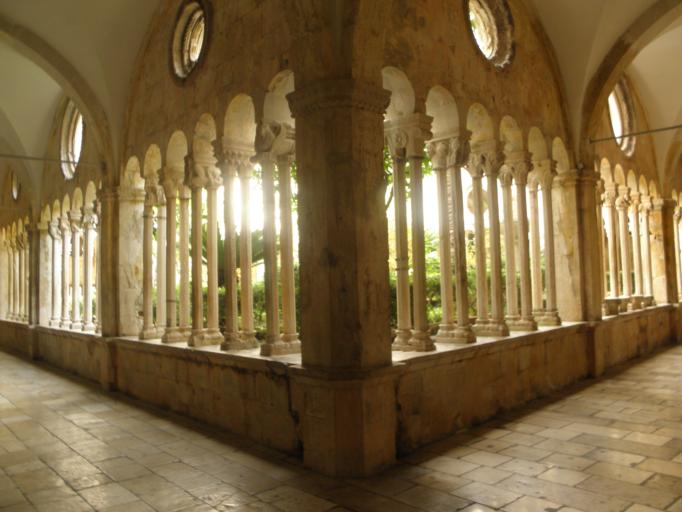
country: HR
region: Dubrovacko-Neretvanska
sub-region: Grad Dubrovnik
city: Dubrovnik
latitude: 42.6416
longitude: 18.1074
